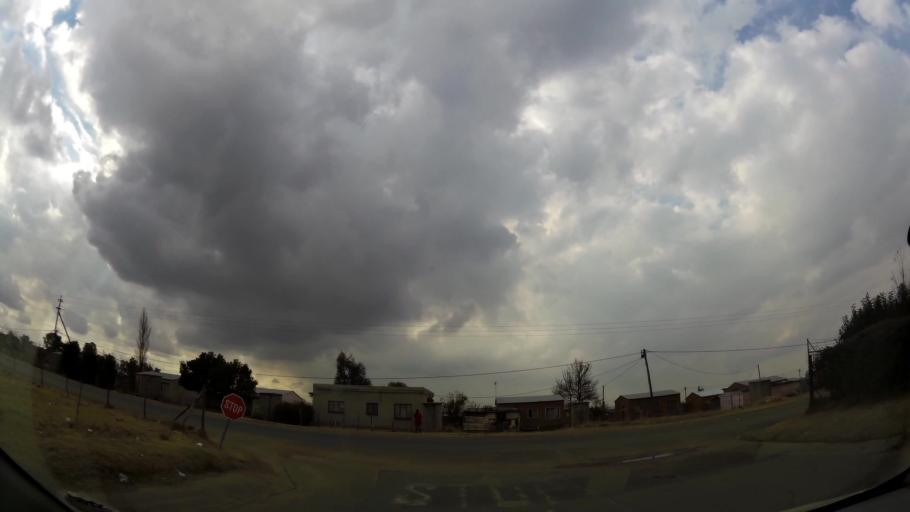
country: ZA
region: Orange Free State
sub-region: Fezile Dabi District Municipality
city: Sasolburg
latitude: -26.8487
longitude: 27.8781
